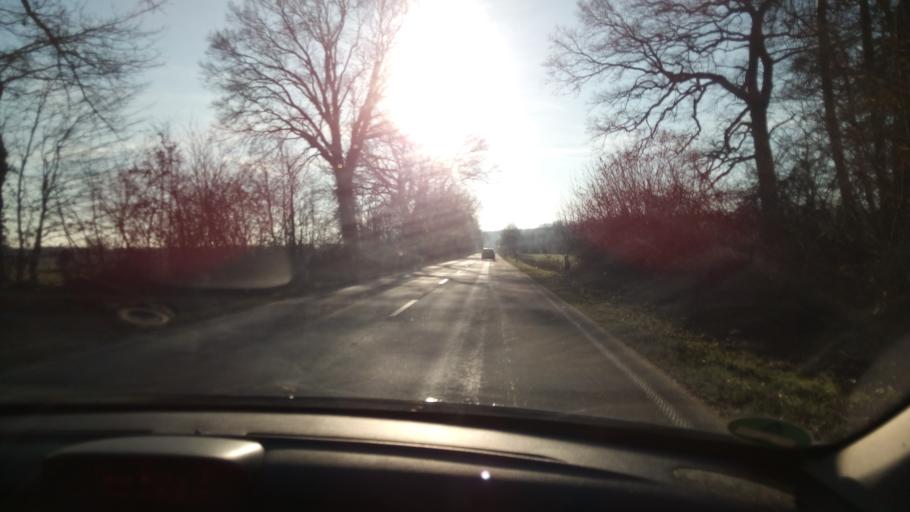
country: DE
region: Schleswig-Holstein
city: Dalldorf
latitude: 53.4370
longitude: 10.6047
